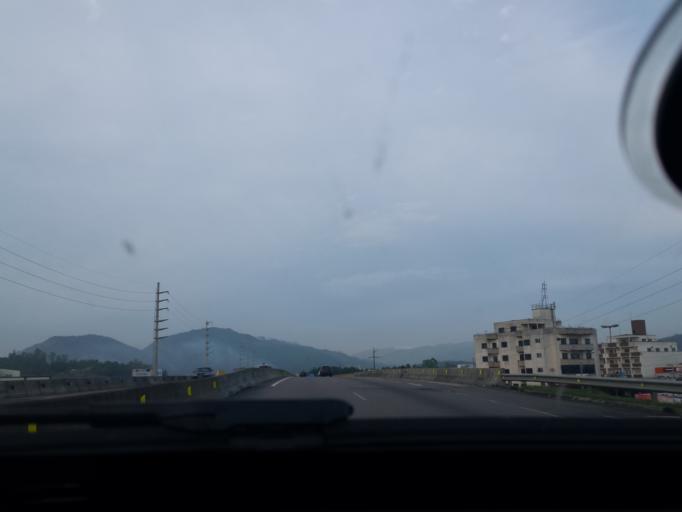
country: BR
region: Santa Catarina
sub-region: Tubarao
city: Tubarao
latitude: -28.4693
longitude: -49.0146
